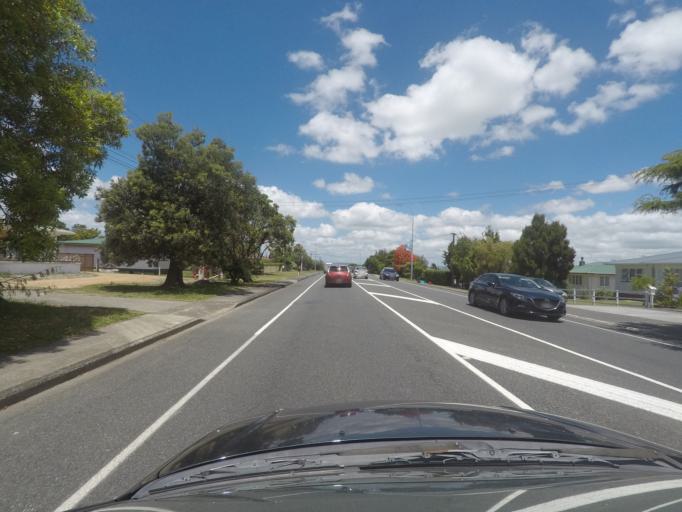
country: NZ
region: Northland
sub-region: Whangarei
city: Whangarei
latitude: -35.7482
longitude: 174.3674
